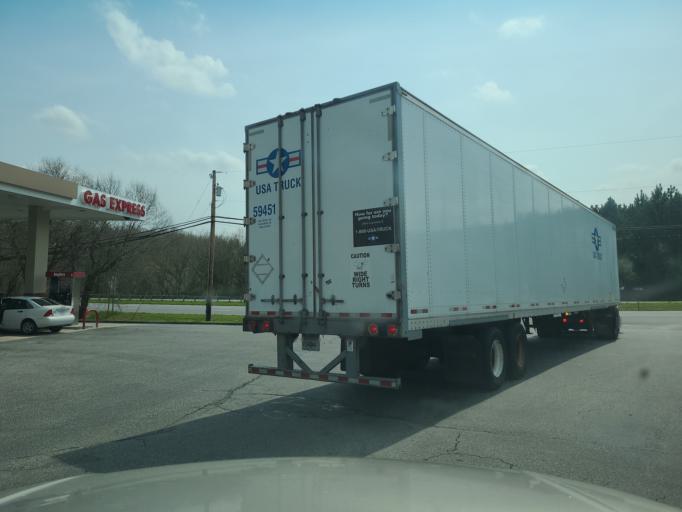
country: US
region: North Carolina
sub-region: Cleveland County
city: Shelby
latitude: 35.2954
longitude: -81.5724
